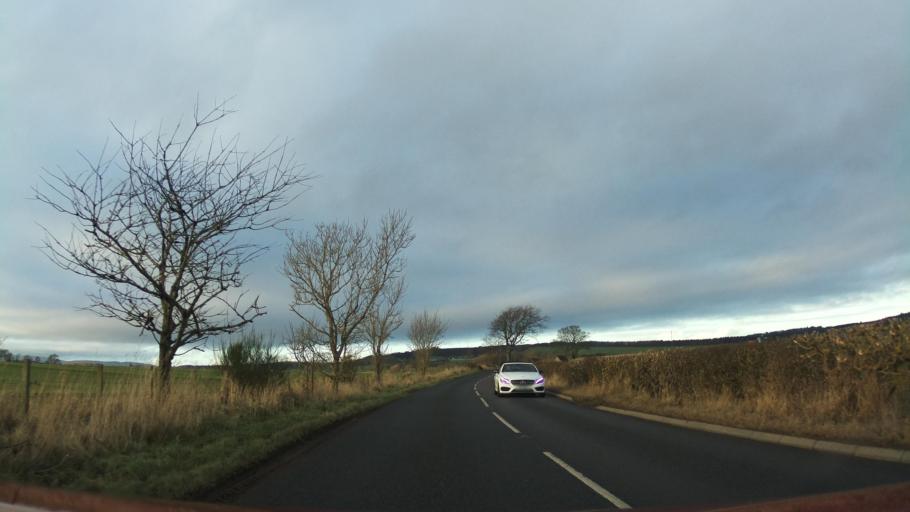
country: GB
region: Scotland
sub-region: Fife
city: Tayport
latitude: 56.5064
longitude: -2.8153
